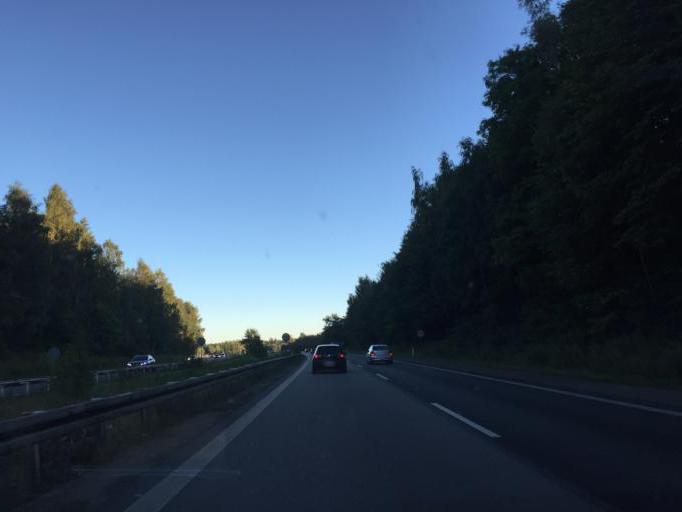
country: DK
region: Capital Region
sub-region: Fureso Kommune
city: Vaerlose
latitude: 55.7846
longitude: 12.3916
